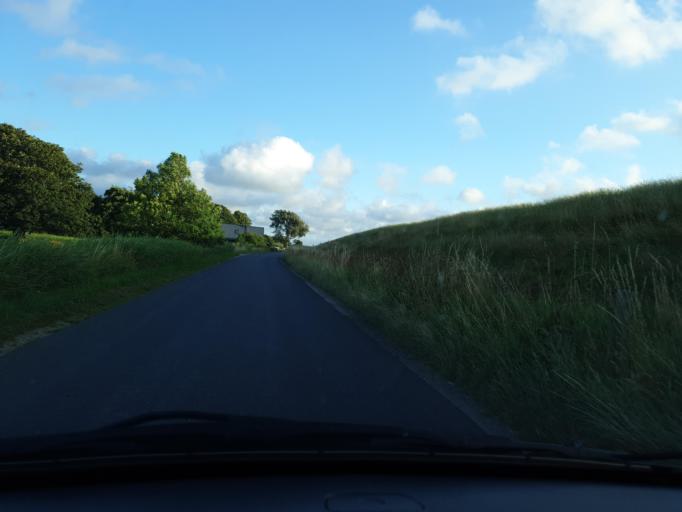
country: DE
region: Schleswig-Holstein
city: Elpersbuttel
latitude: 54.0857
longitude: 9.0304
